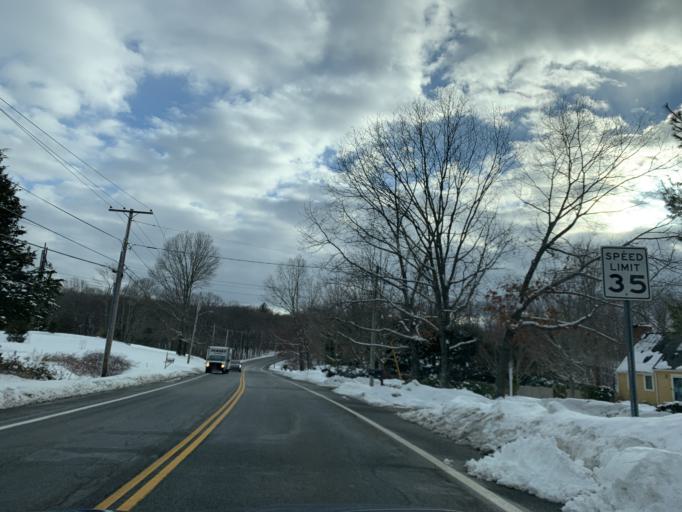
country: US
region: Rhode Island
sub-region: Providence County
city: Cumberland Hill
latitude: 42.0044
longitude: -71.4539
